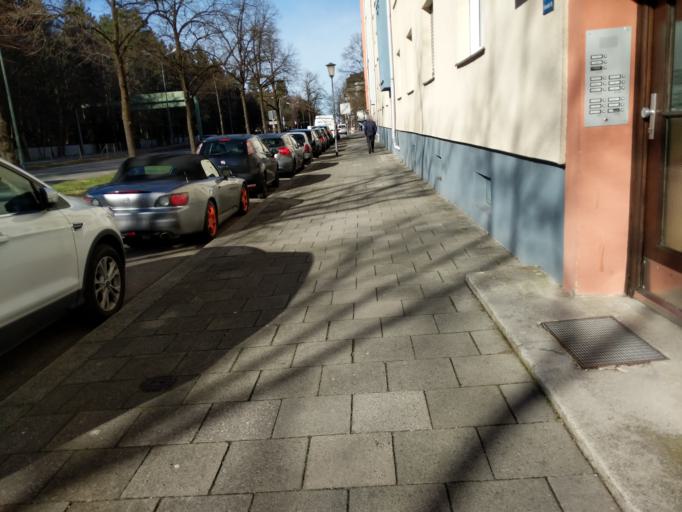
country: DE
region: Bavaria
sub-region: Upper Bavaria
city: Neuried
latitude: 48.1059
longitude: 11.5024
